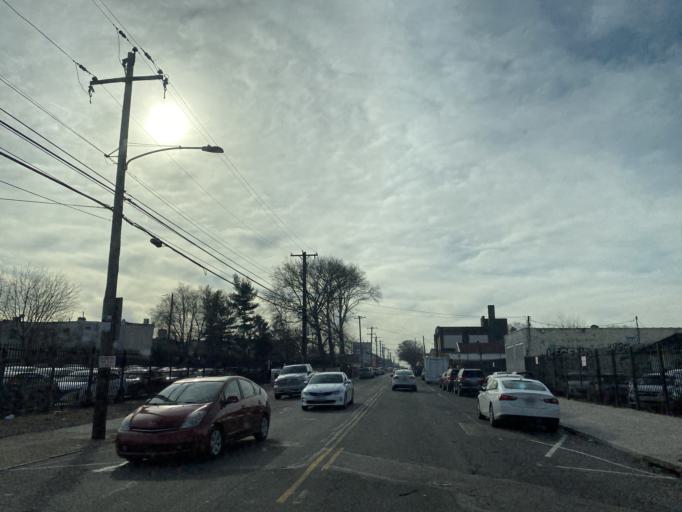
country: US
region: New Jersey
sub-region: Camden County
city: Pennsauken
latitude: 40.0051
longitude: -75.0930
